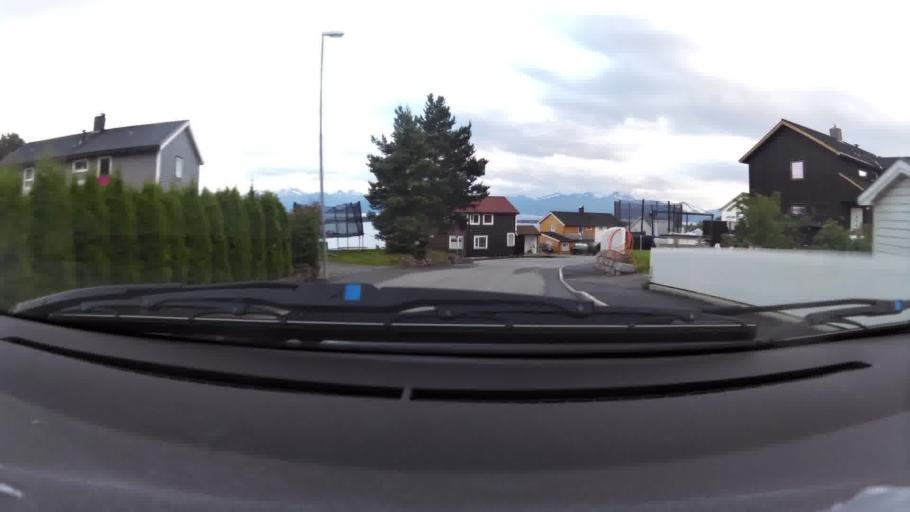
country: NO
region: More og Romsdal
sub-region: Molde
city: Molde
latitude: 62.7421
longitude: 7.1869
